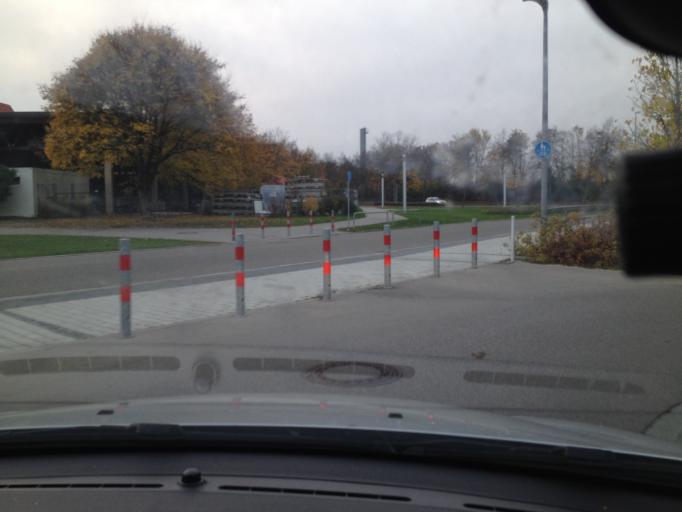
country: DE
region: Bavaria
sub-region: Swabia
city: Konigsbrunn
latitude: 48.2720
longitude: 10.8875
